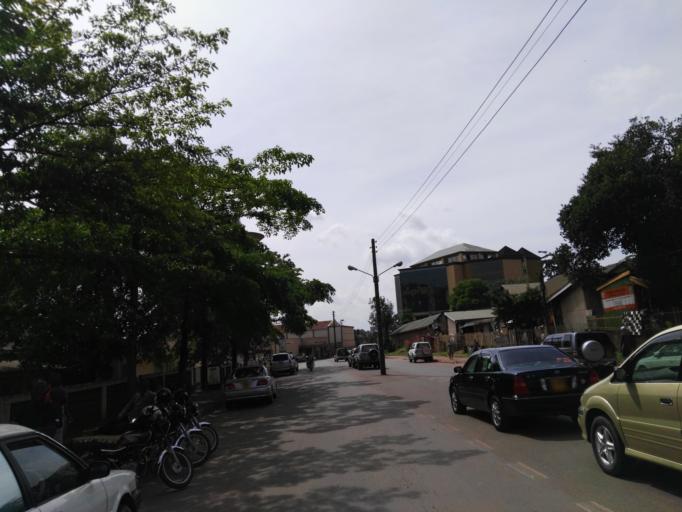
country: UG
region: Central Region
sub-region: Kampala District
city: Kampala
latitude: 0.3177
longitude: 32.5762
